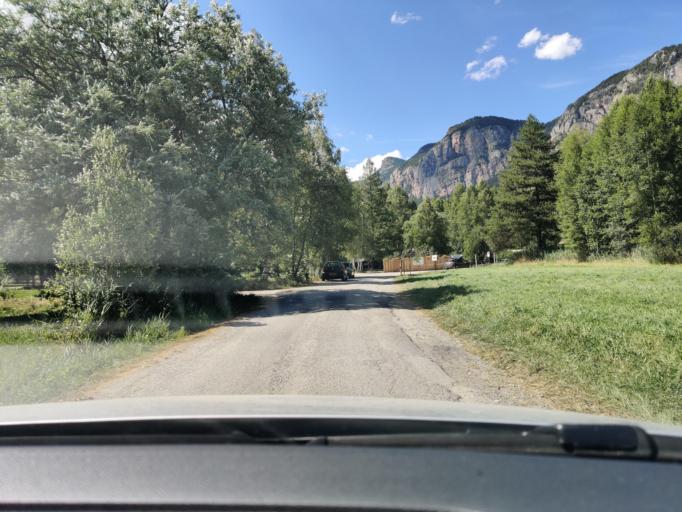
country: FR
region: Provence-Alpes-Cote d'Azur
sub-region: Departement des Hautes-Alpes
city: Saint-Martin-de-Queyrieres
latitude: 44.7409
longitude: 6.5621
